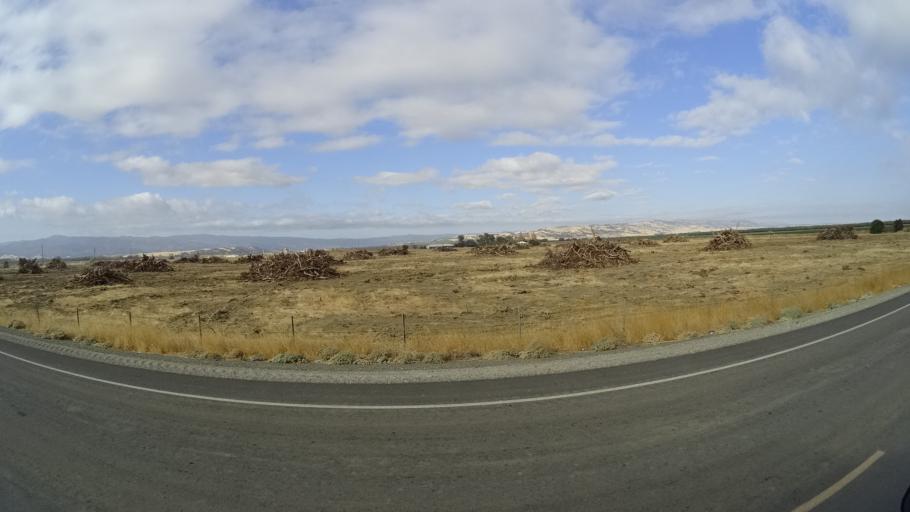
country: US
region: California
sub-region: Yolo County
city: Esparto
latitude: 38.7167
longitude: -122.0100
